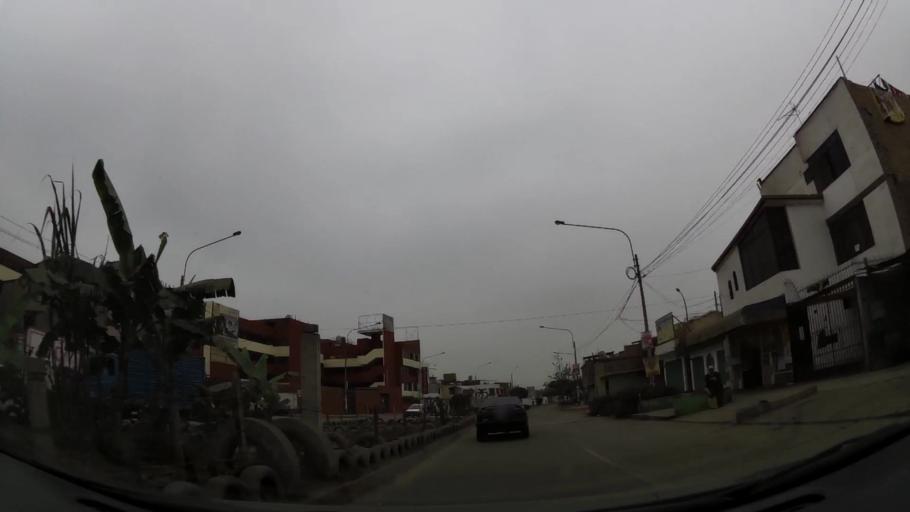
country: PE
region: Lima
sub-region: Lima
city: Urb. Santo Domingo
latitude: -11.8927
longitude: -77.0393
